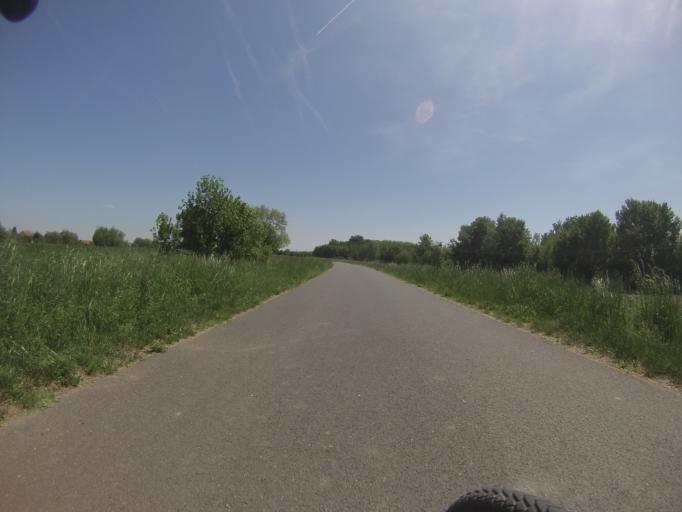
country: CZ
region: South Moravian
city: Vranovice
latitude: 48.9263
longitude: 16.5735
